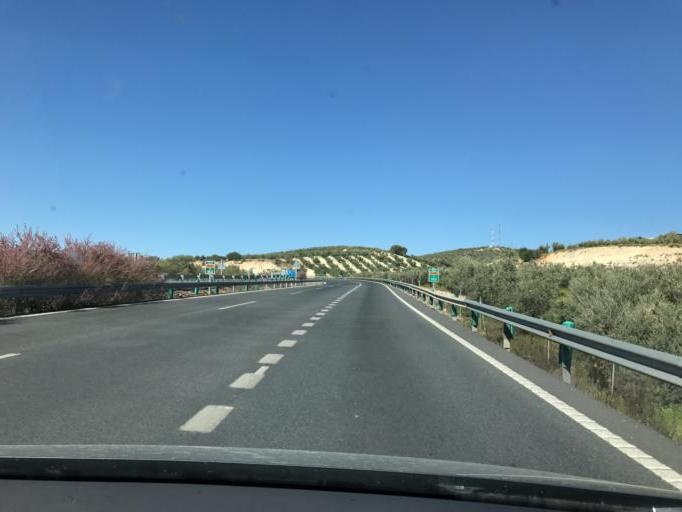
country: ES
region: Andalusia
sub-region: Provincia de Granada
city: Loja
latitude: 37.1488
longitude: -4.2294
